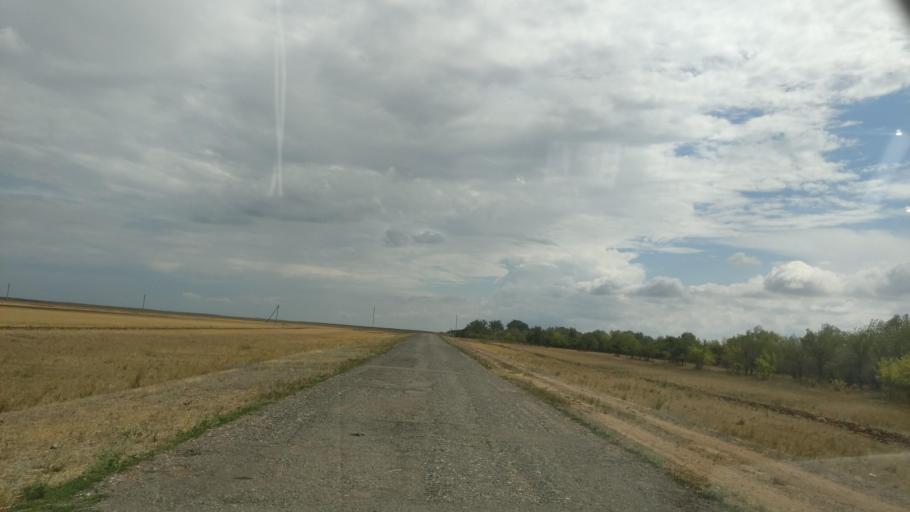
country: KZ
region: Pavlodar
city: Pavlodar
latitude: 52.6438
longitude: 77.0427
